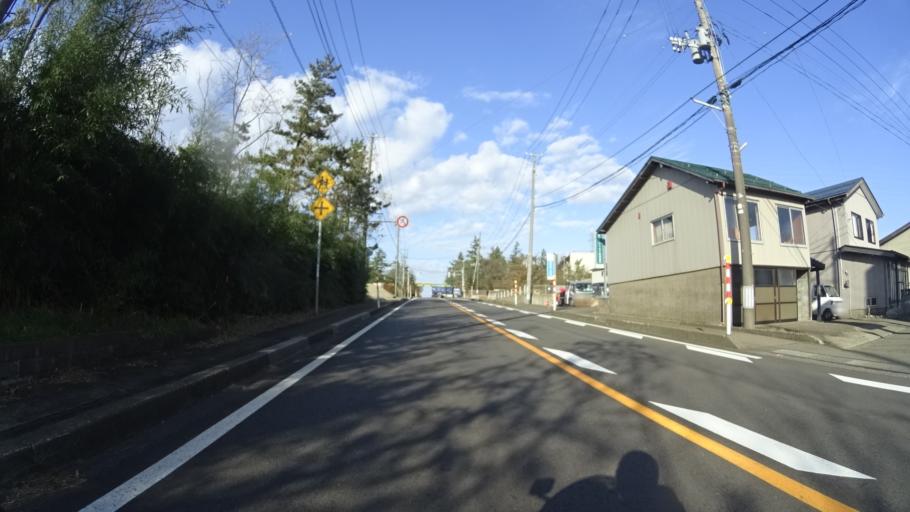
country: JP
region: Niigata
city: Kashiwazaki
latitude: 37.2810
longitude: 138.3978
